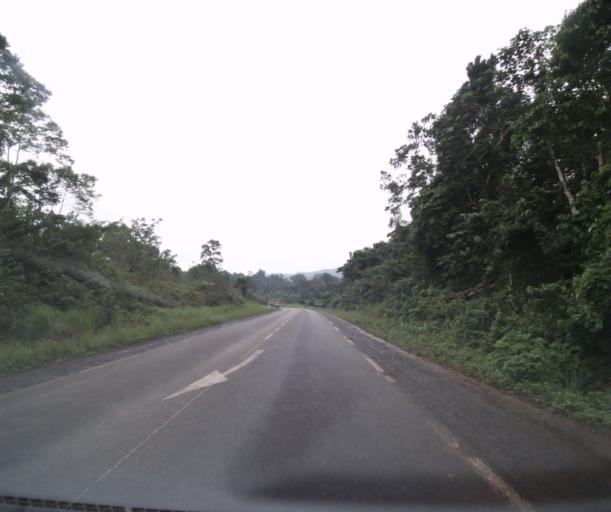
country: CM
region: Littoral
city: Edea
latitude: 3.8330
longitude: 10.4061
